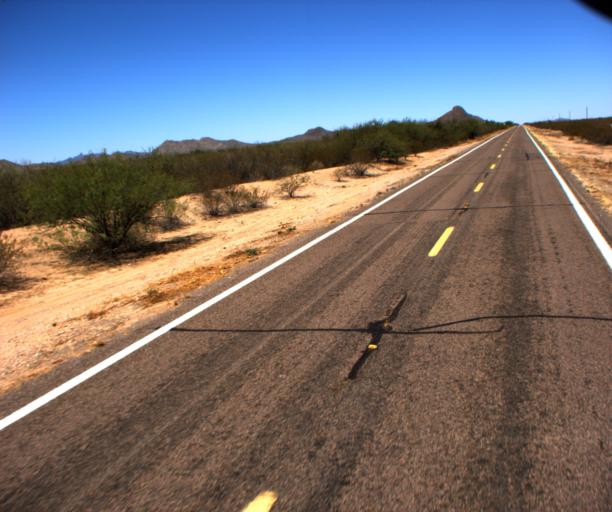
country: US
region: Arizona
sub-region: Pima County
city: Ajo
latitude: 32.2003
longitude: -112.4951
